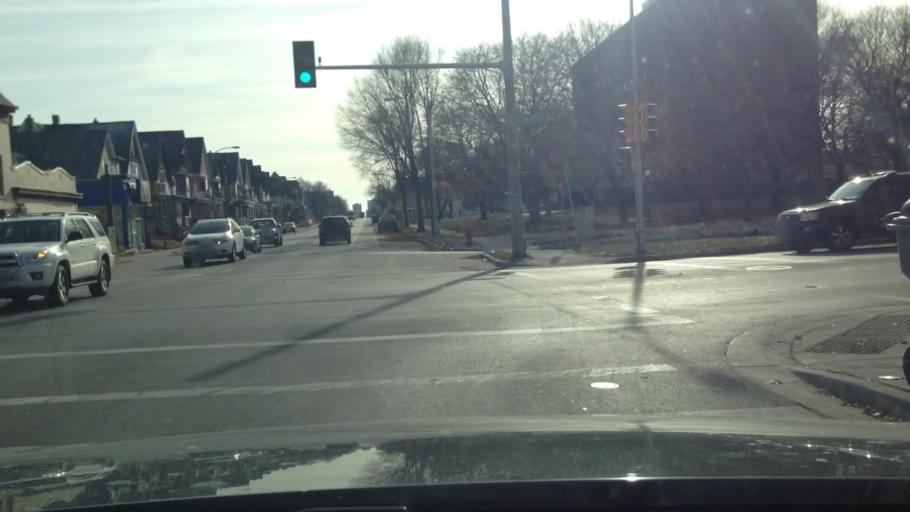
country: US
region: Wisconsin
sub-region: Milwaukee County
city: Shorewood
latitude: 43.0712
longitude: -87.9053
